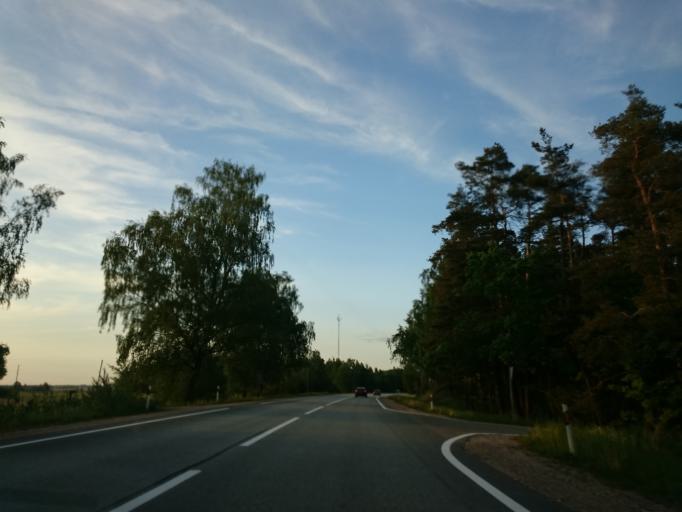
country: LV
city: Tireli
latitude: 56.8773
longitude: 23.6296
